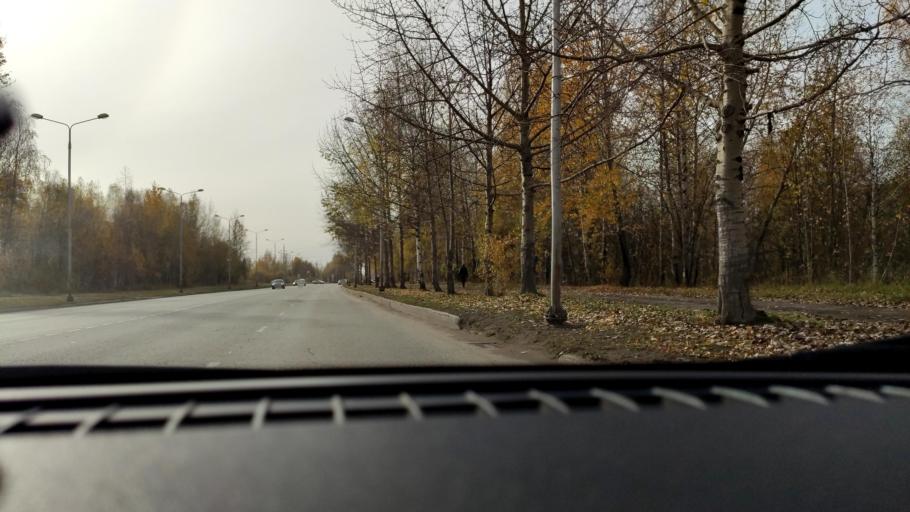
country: RU
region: Perm
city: Perm
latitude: 58.1032
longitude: 56.3917
